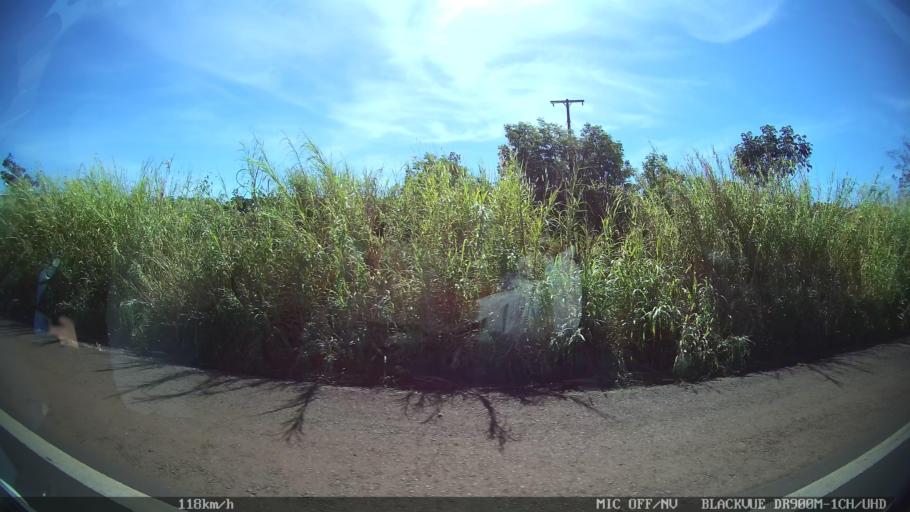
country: BR
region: Sao Paulo
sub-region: Franca
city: Franca
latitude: -20.5556
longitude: -47.5858
